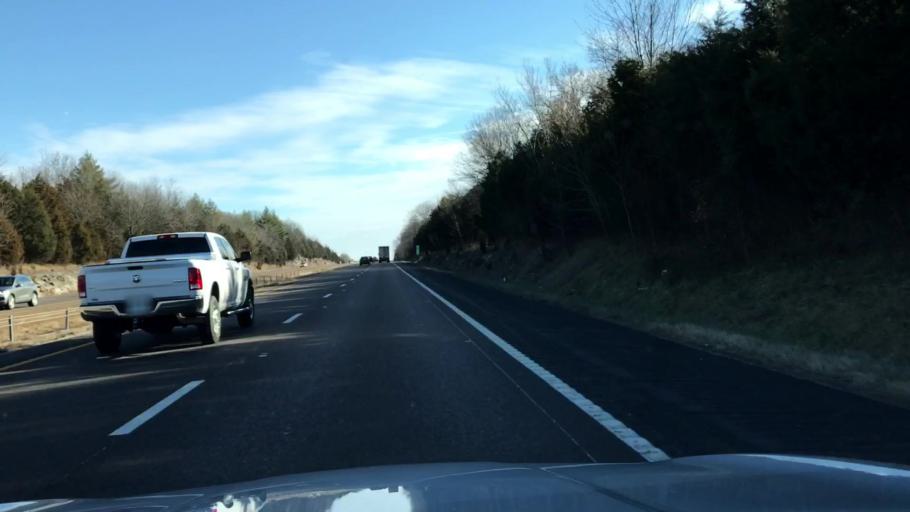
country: US
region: Missouri
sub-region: Boone County
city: Columbia
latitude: 38.9727
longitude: -92.4678
